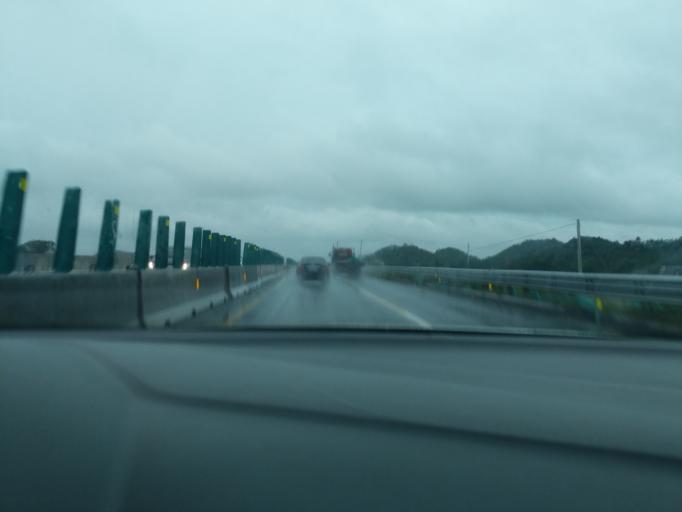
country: CN
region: Guangdong
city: Yueshan
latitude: 22.4627
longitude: 112.7187
